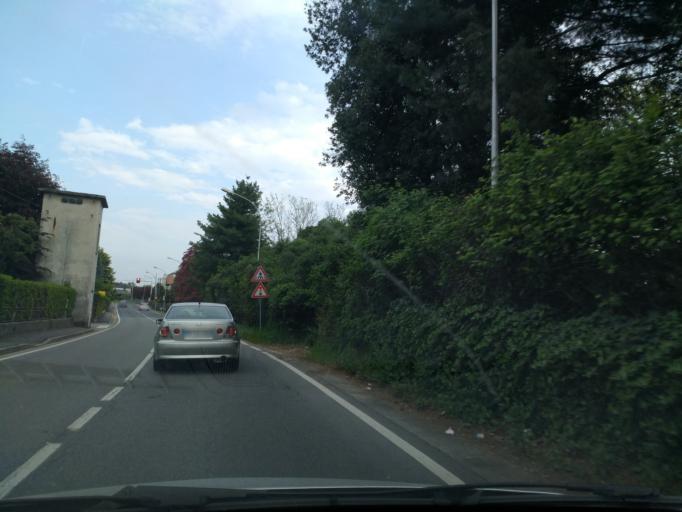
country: IT
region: Lombardy
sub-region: Provincia di Como
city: Figino Serenza
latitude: 45.7162
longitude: 9.1375
